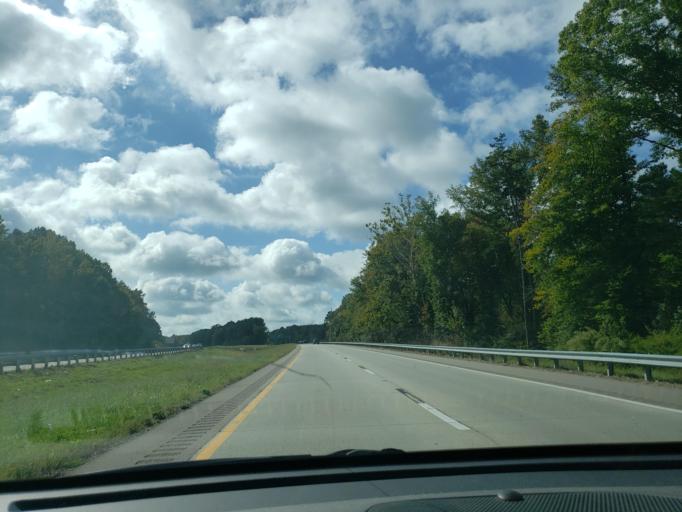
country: US
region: North Carolina
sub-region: Vance County
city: Henderson
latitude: 36.3395
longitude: -78.4238
